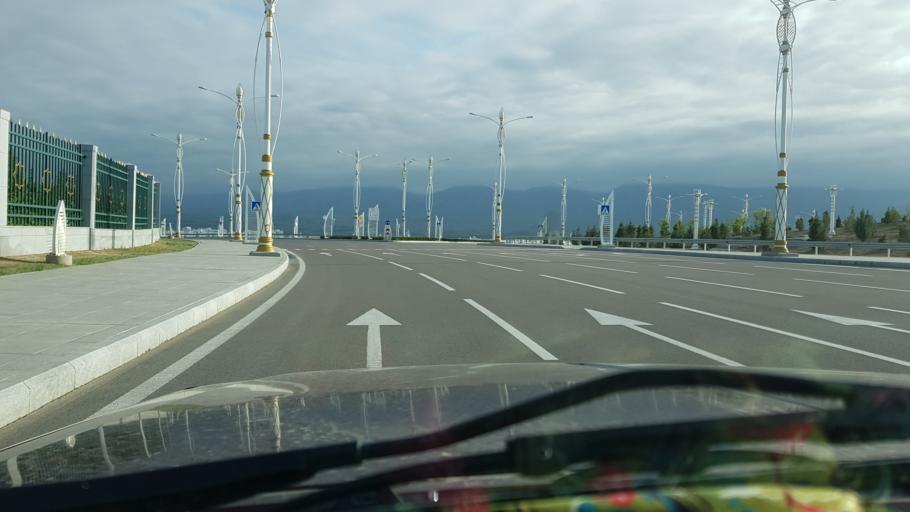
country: TM
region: Ahal
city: Ashgabat
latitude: 37.9300
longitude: 58.3317
